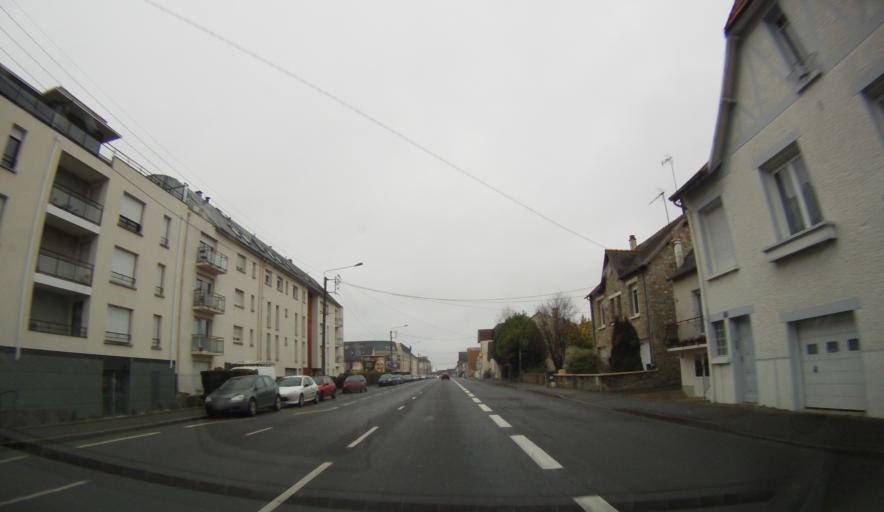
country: FR
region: Brittany
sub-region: Departement d'Ille-et-Vilaine
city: Rennes
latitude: 48.0932
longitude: -1.6479
